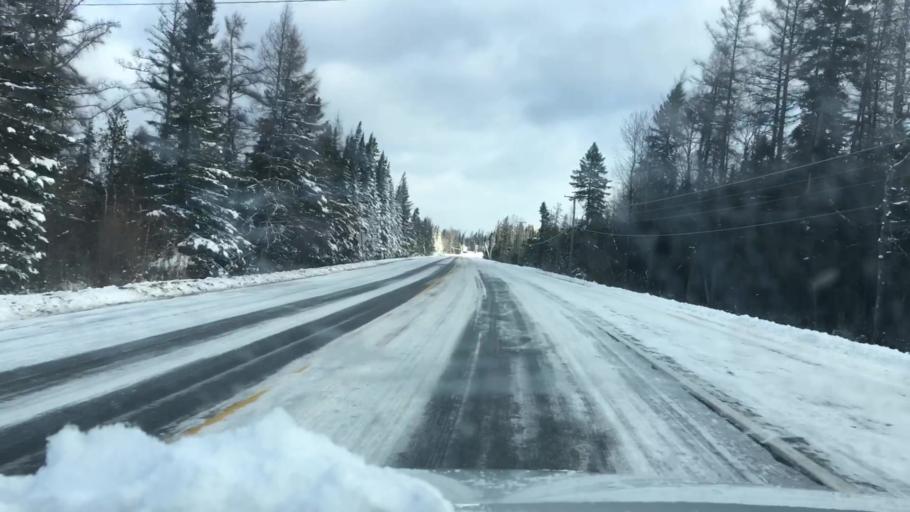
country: US
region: Maine
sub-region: Aroostook County
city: Madawaska
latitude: 47.0003
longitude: -68.0243
